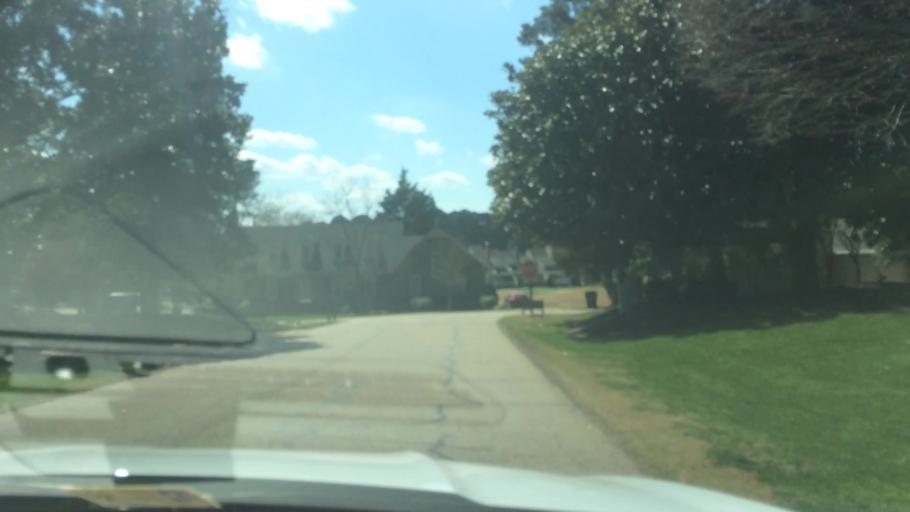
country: US
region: Virginia
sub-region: City of Williamsburg
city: Williamsburg
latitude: 37.2296
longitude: -76.6792
